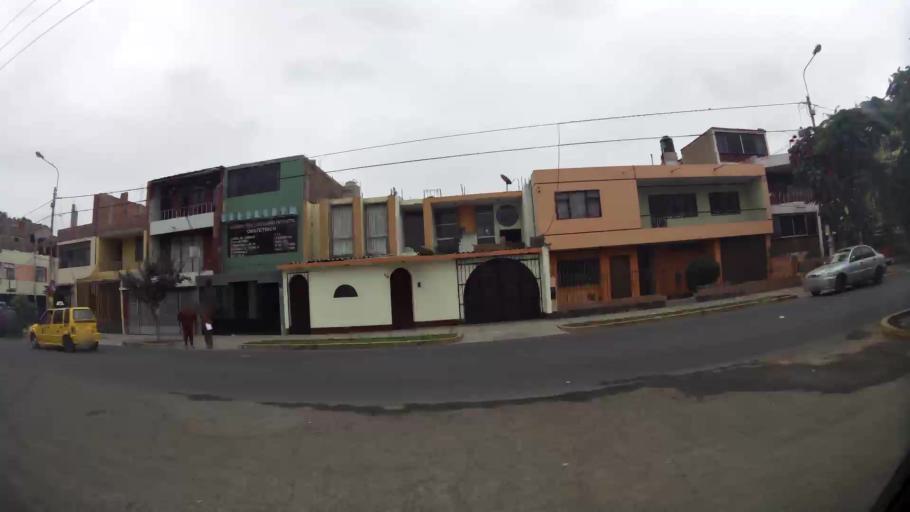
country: PE
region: La Libertad
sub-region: Provincia de Trujillo
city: Trujillo
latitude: -8.1177
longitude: -79.0284
